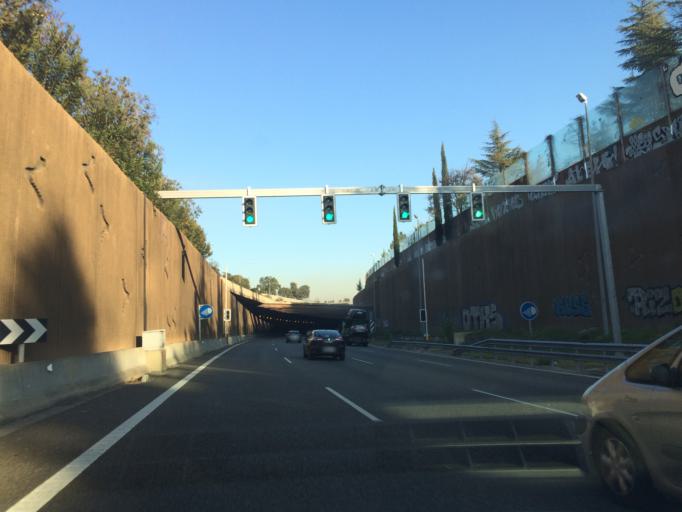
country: ES
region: Madrid
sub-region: Provincia de Madrid
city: El Pardo
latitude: 40.4740
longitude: -3.7818
